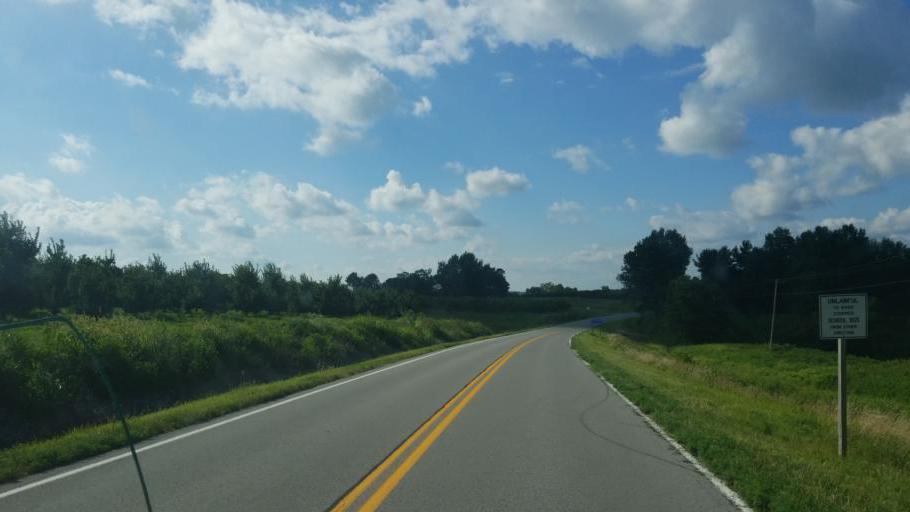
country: US
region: Illinois
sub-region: Union County
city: Cobden
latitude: 37.5852
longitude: -89.3231
